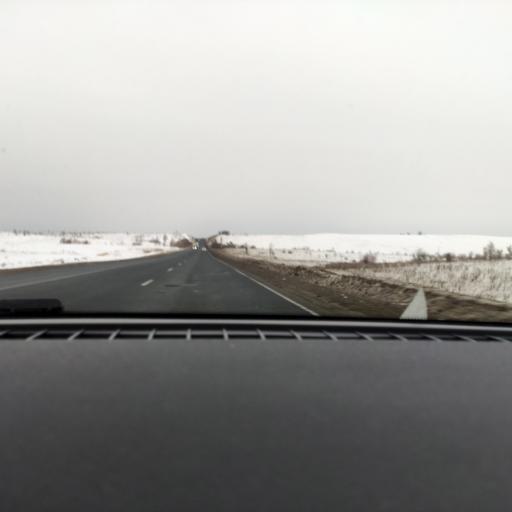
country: RU
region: Samara
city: Novosemeykino
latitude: 53.4034
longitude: 50.3882
